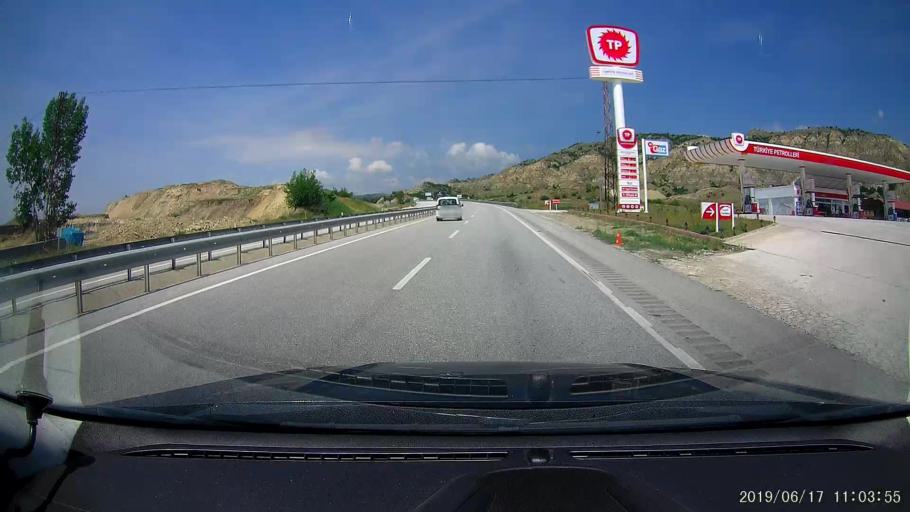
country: TR
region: Kastamonu
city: Tosya
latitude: 41.0200
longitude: 34.1062
